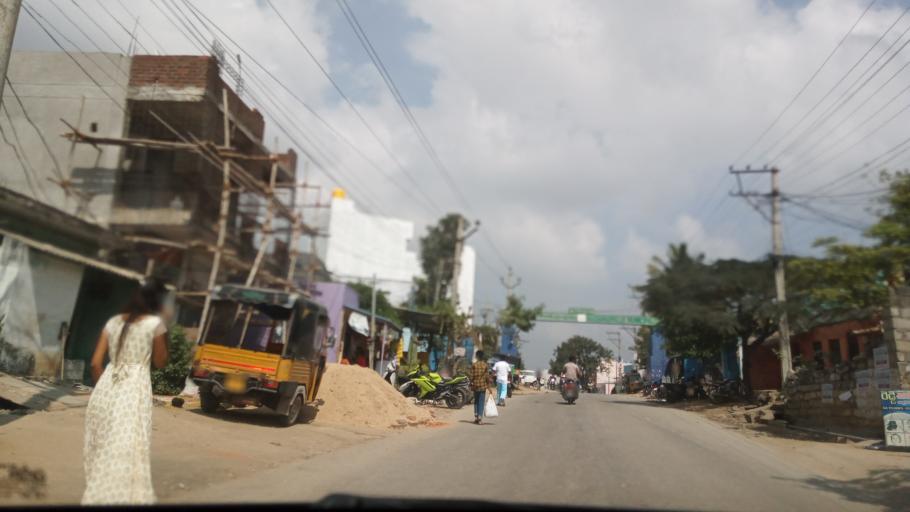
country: IN
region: Andhra Pradesh
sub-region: Chittoor
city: Madanapalle
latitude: 13.5665
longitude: 78.5135
